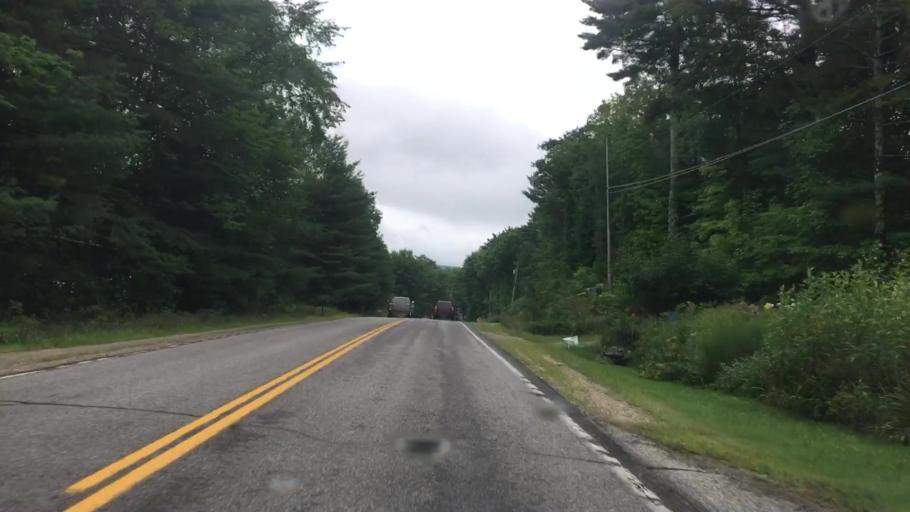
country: US
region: Maine
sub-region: Oxford County
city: Brownfield
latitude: 43.9548
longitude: -70.8966
